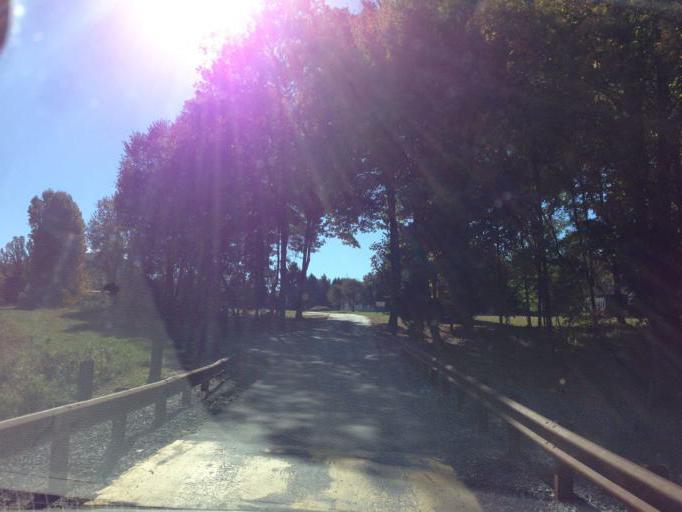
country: US
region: Maryland
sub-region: Howard County
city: Fulton
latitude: 39.1504
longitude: -76.8987
